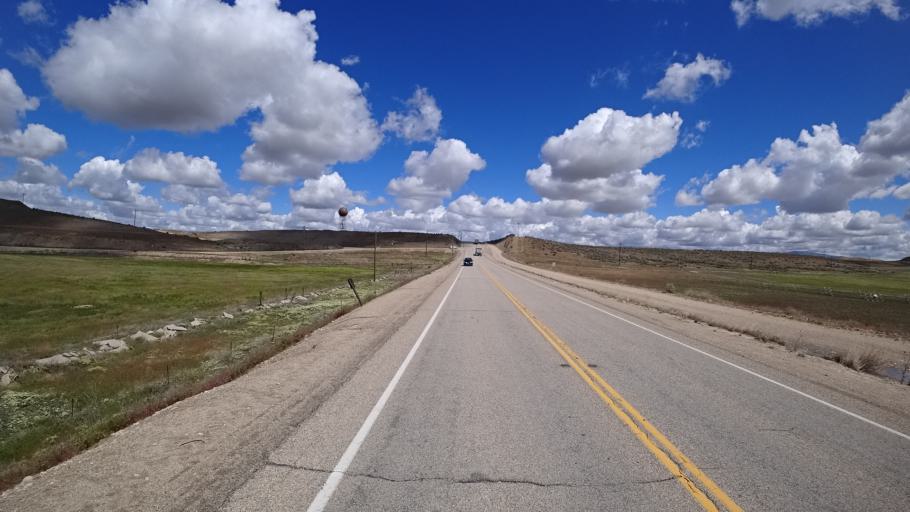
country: US
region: Idaho
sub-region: Ada County
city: Boise
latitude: 43.4865
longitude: -116.2341
